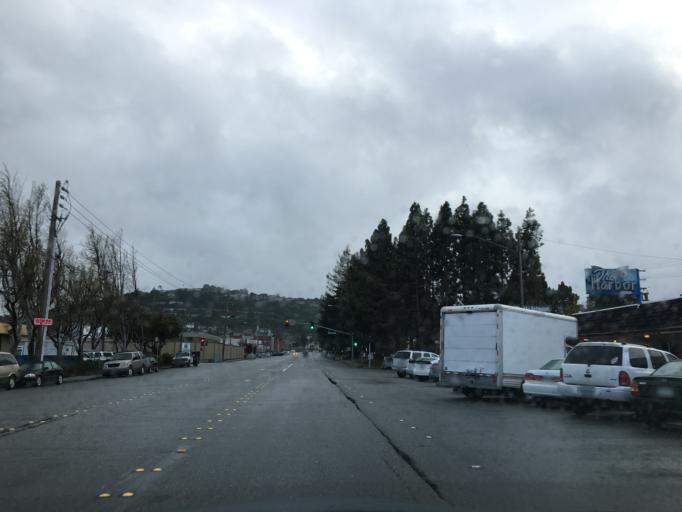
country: US
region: California
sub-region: San Mateo County
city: Belmont
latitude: 37.5218
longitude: -122.2666
